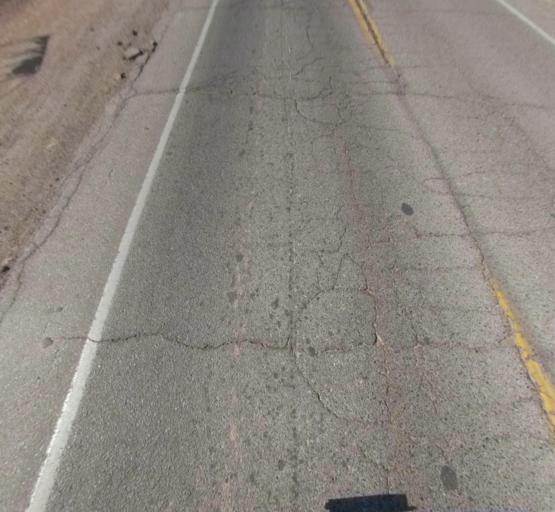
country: US
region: California
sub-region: Madera County
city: Chowchilla
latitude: 37.1446
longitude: -120.2744
